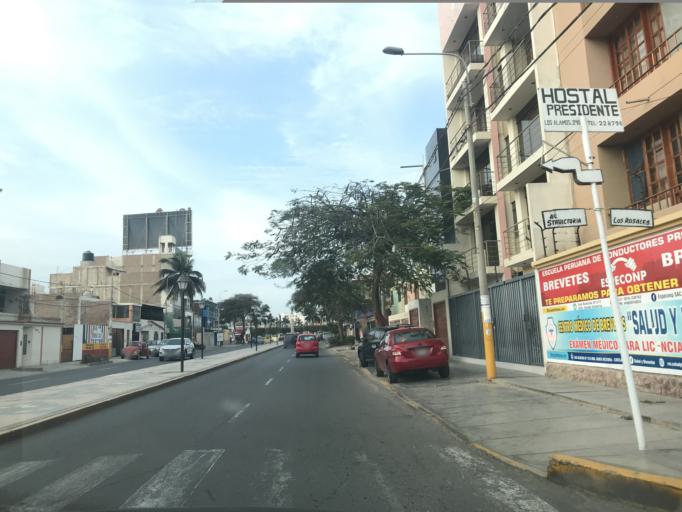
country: PE
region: Lambayeque
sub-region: Provincia de Chiclayo
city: Chiclayo
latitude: -6.7837
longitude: -79.8432
